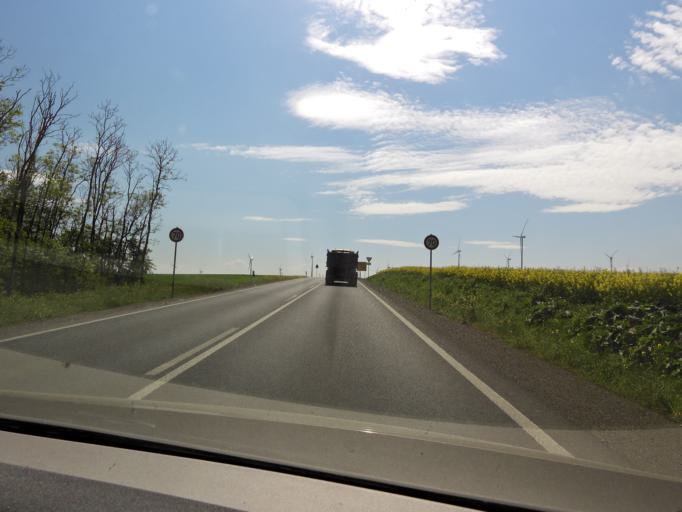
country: DE
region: Thuringia
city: Hochheim
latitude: 51.0548
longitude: 10.6524
